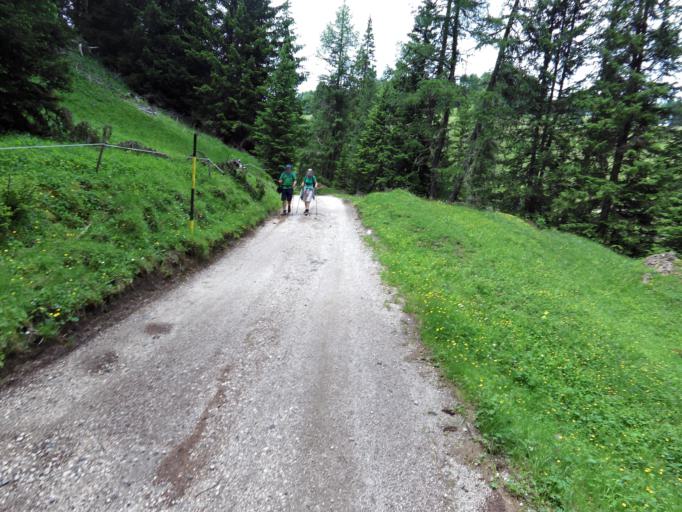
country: IT
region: Trentino-Alto Adige
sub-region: Bolzano
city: Ortisei
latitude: 46.5325
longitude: 11.6480
